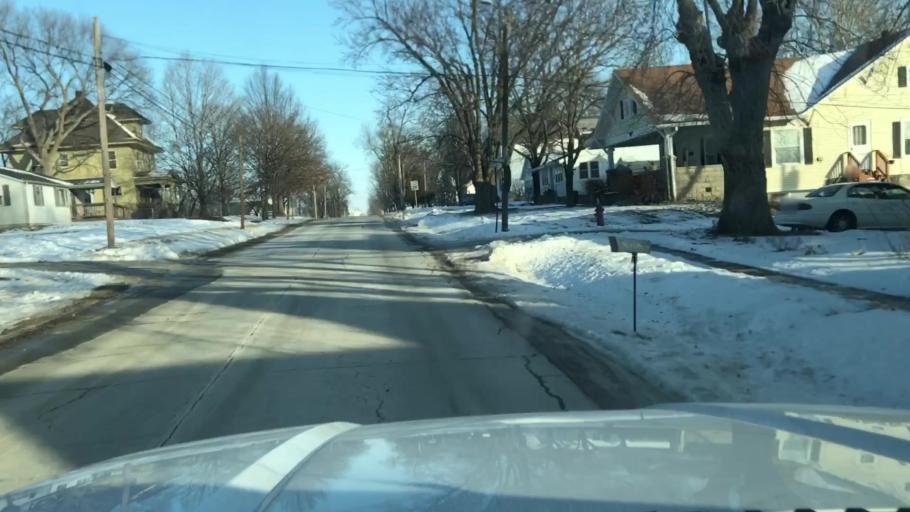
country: US
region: Missouri
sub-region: Andrew County
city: Savannah
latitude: 40.0251
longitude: -94.9718
